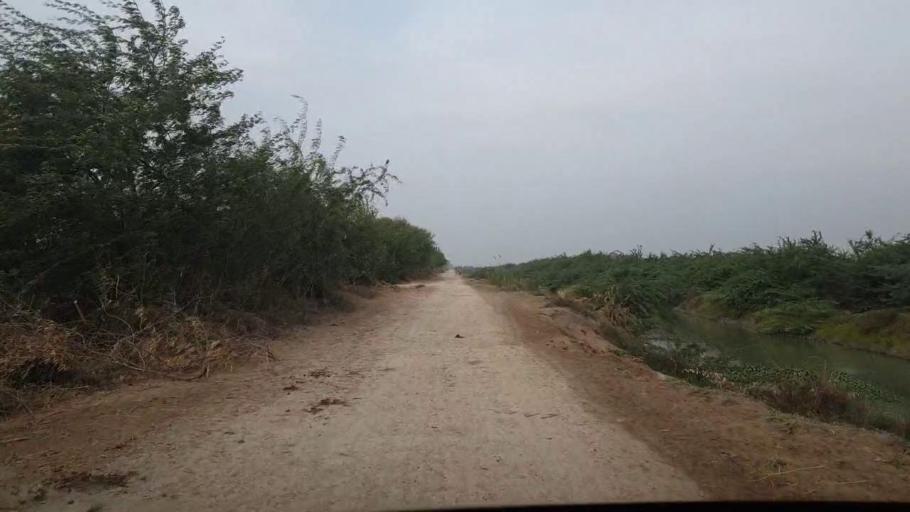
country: PK
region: Sindh
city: Chuhar Jamali
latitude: 24.4075
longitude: 67.9531
